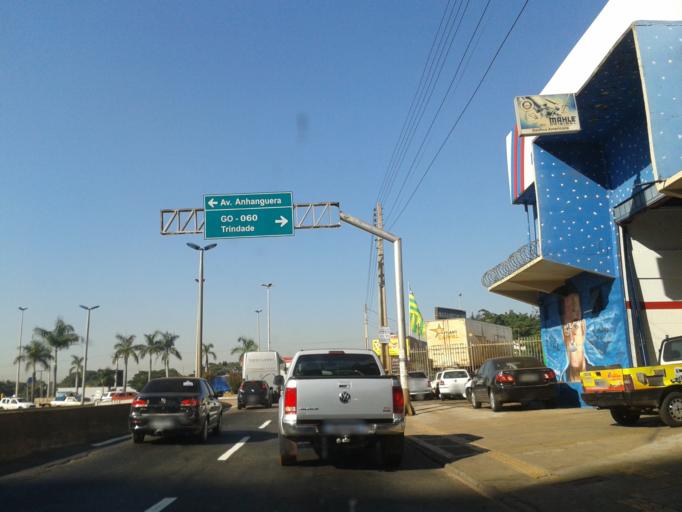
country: BR
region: Goias
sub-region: Goiania
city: Goiania
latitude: -16.6593
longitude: -49.3298
